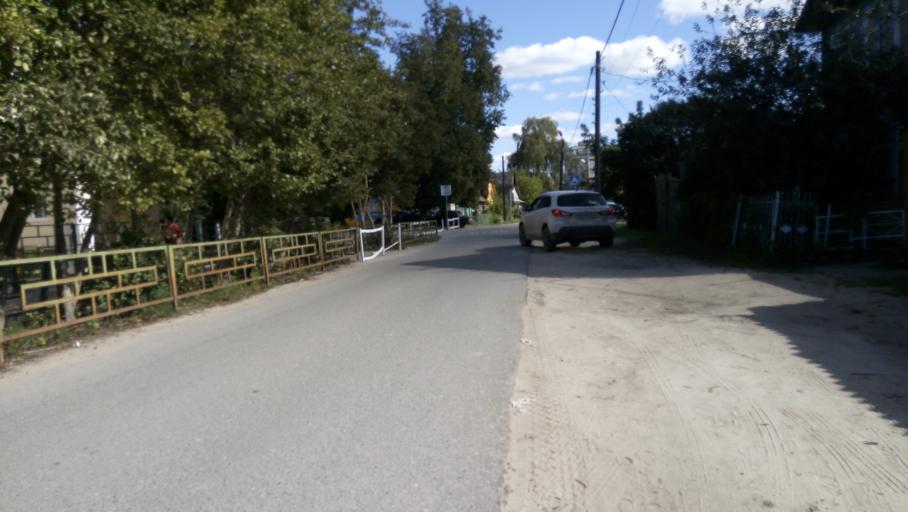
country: RU
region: Nizjnij Novgorod
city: Bor
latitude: 56.3595
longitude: 44.0574
